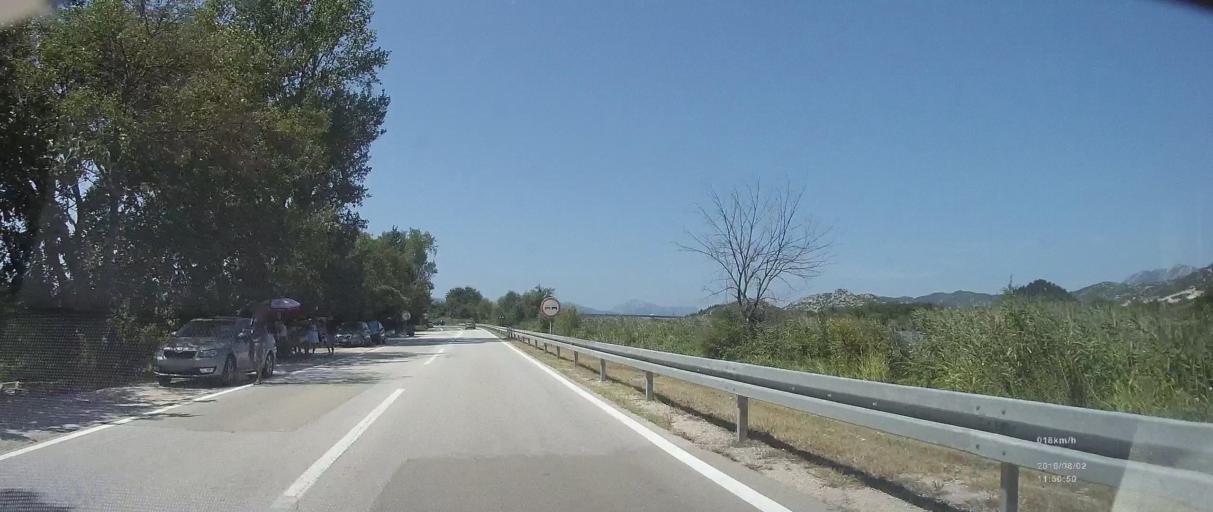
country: HR
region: Dubrovacko-Neretvanska
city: Komin
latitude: 43.0417
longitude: 17.4991
